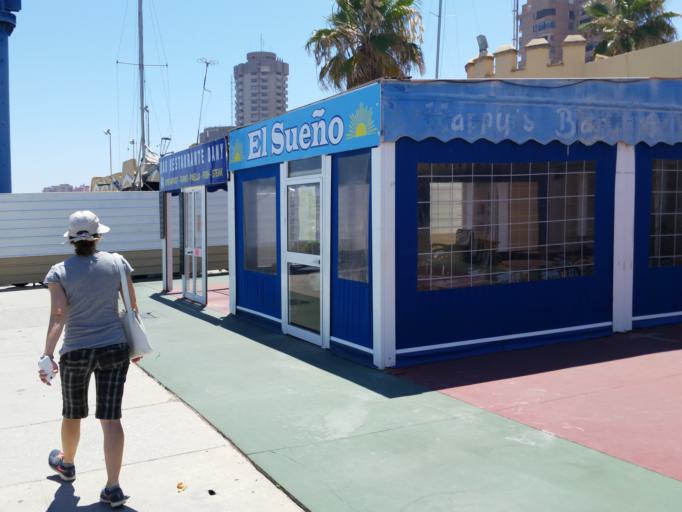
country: ES
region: Andalusia
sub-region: Provincia de Malaga
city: Fuengirola
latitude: 36.5416
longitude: -4.6180
